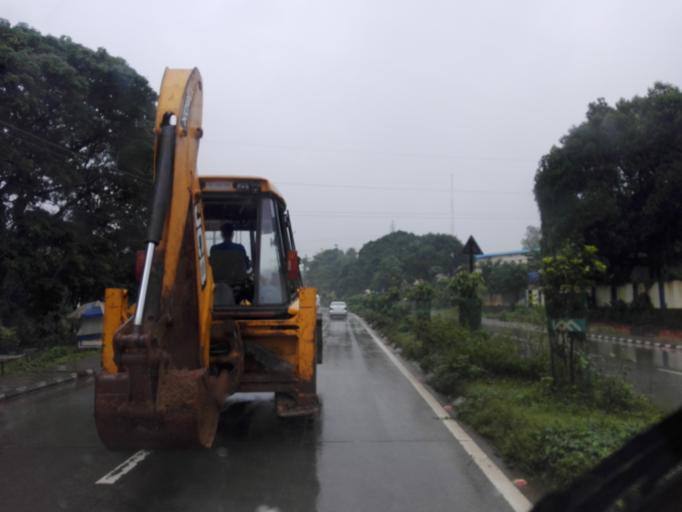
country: IN
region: Kerala
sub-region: Ernakulam
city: Elur
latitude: 10.0533
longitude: 76.3313
